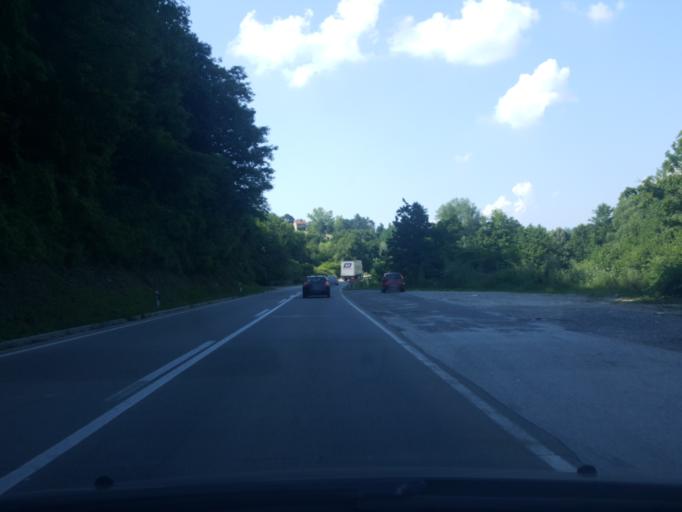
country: RS
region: Central Serbia
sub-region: Moravicki Okrug
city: Gornji Milanovac
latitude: 44.1092
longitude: 20.4833
